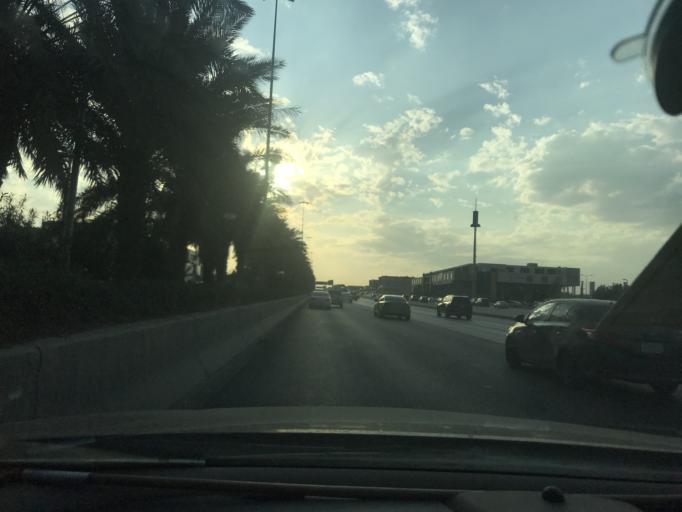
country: SA
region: Ar Riyad
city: Riyadh
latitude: 24.7543
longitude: 46.6313
